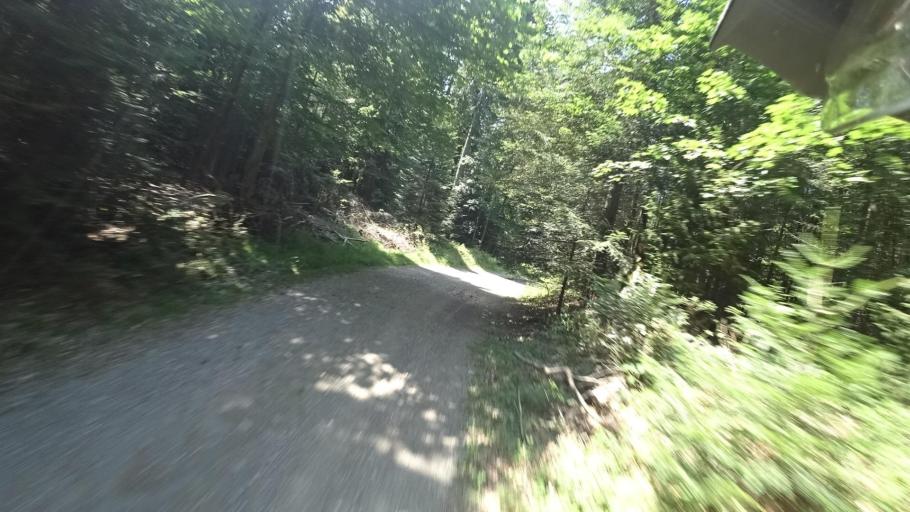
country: HR
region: Primorsko-Goranska
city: Bribir
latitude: 45.2610
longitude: 14.8785
